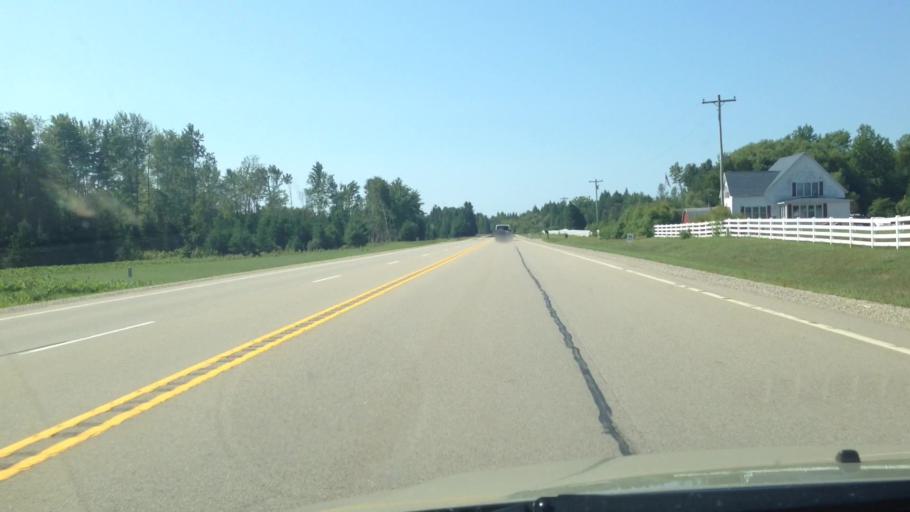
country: US
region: Michigan
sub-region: Delta County
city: Escanaba
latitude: 45.5267
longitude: -87.2873
